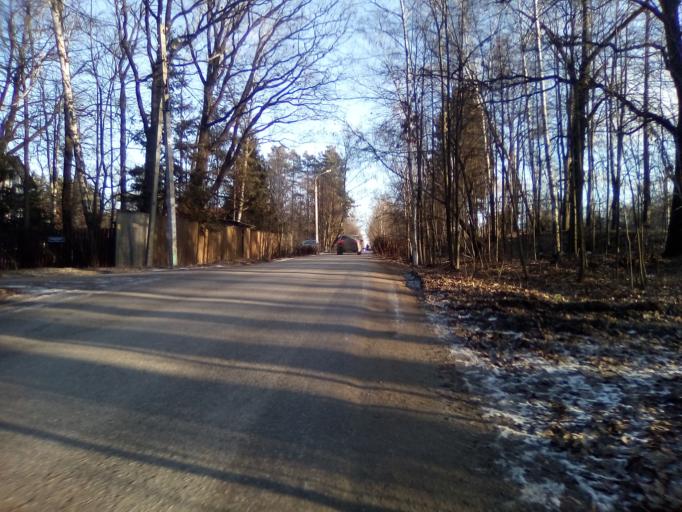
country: RU
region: Moskovskaya
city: Lesnoy Gorodok
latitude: 55.6653
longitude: 37.2091
